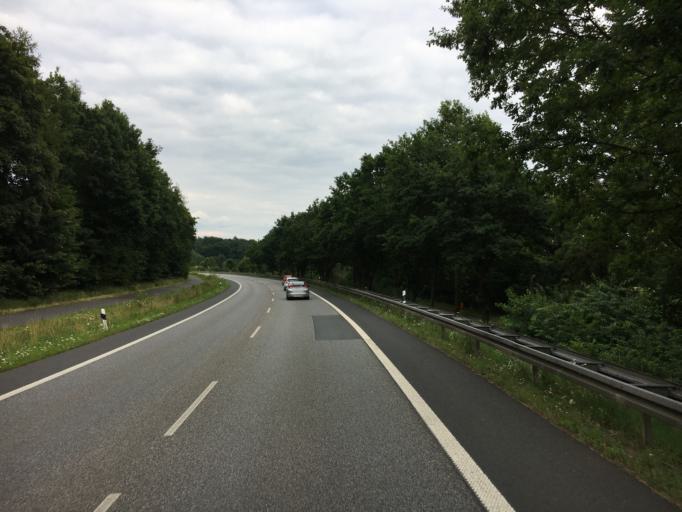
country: DE
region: Hesse
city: Stadtallendorf
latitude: 50.8236
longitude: 8.9785
